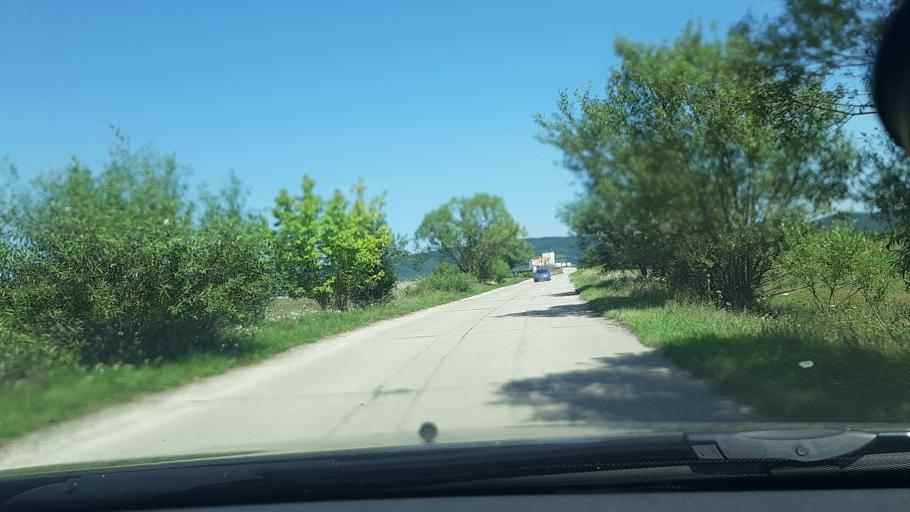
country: RO
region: Hunedoara
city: Bucium-Orlea
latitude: 45.5874
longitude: 22.9598
